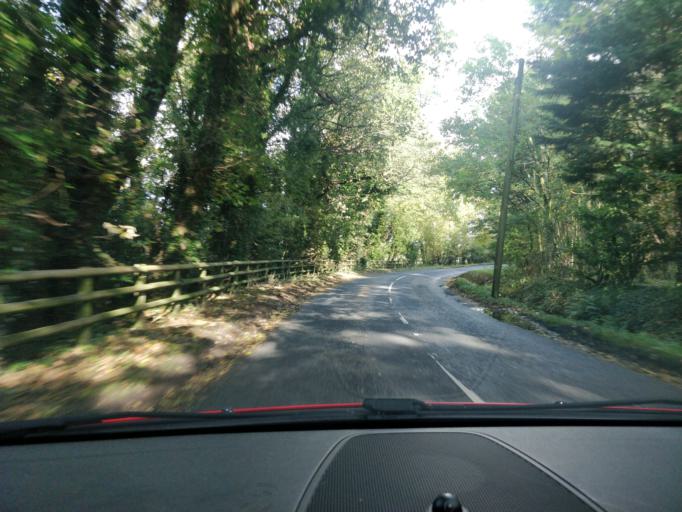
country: GB
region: England
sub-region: Lancashire
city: Ormskirk
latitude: 53.5832
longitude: -2.8486
